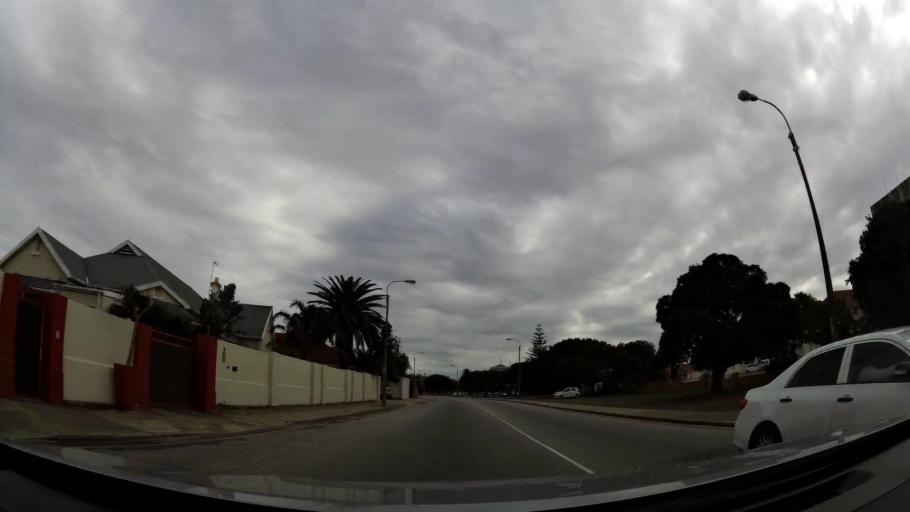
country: ZA
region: Eastern Cape
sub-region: Nelson Mandela Bay Metropolitan Municipality
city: Port Elizabeth
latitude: -33.9595
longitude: 25.5996
